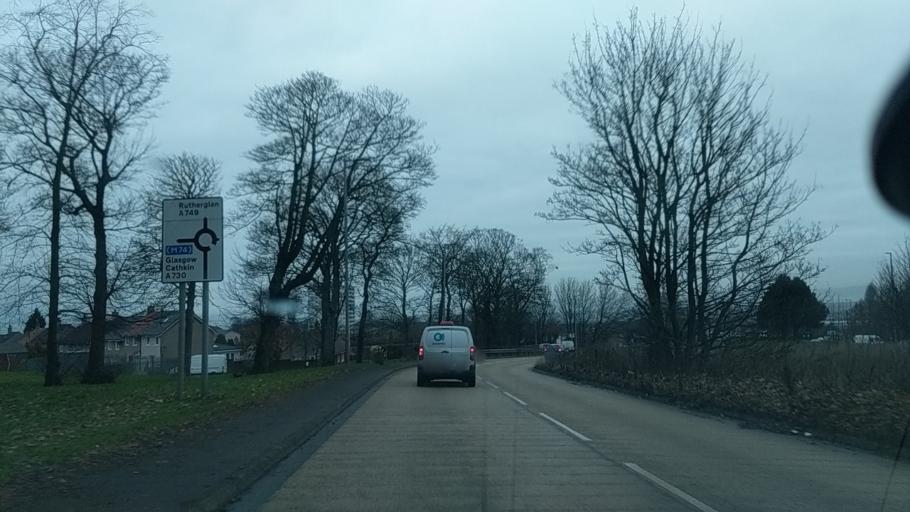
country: GB
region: Scotland
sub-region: South Lanarkshire
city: Rutherglen
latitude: 55.8051
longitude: -4.1841
